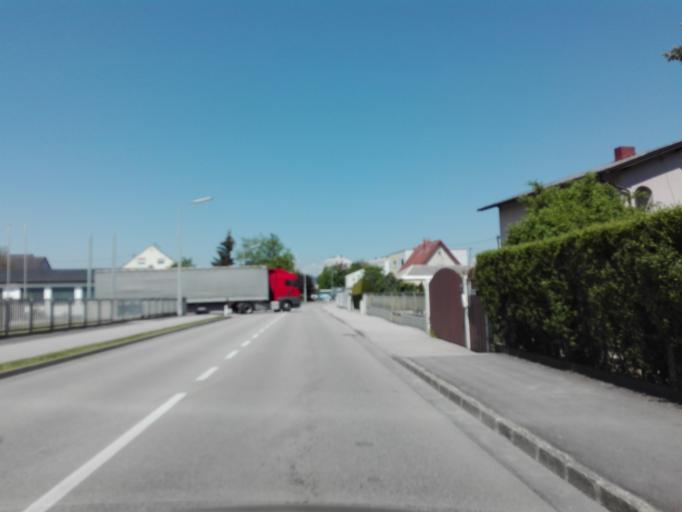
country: AT
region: Upper Austria
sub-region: Politischer Bezirk Linz-Land
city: Traun
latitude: 48.2414
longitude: 14.2602
